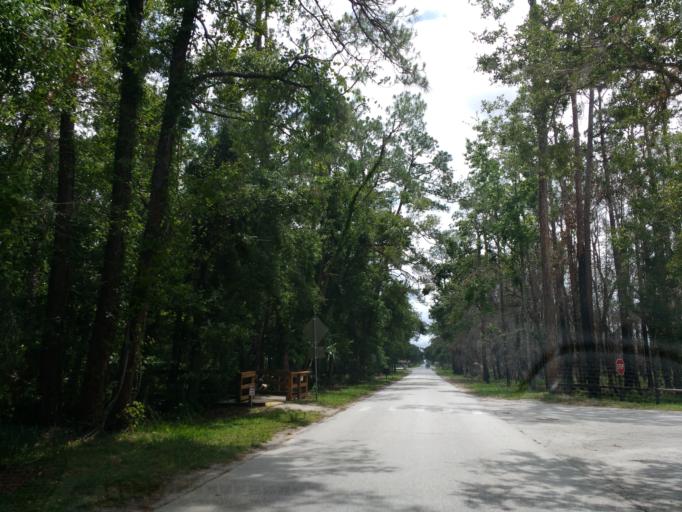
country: US
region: Florida
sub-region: Highlands County
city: Sebring
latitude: 27.4710
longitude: -81.5327
